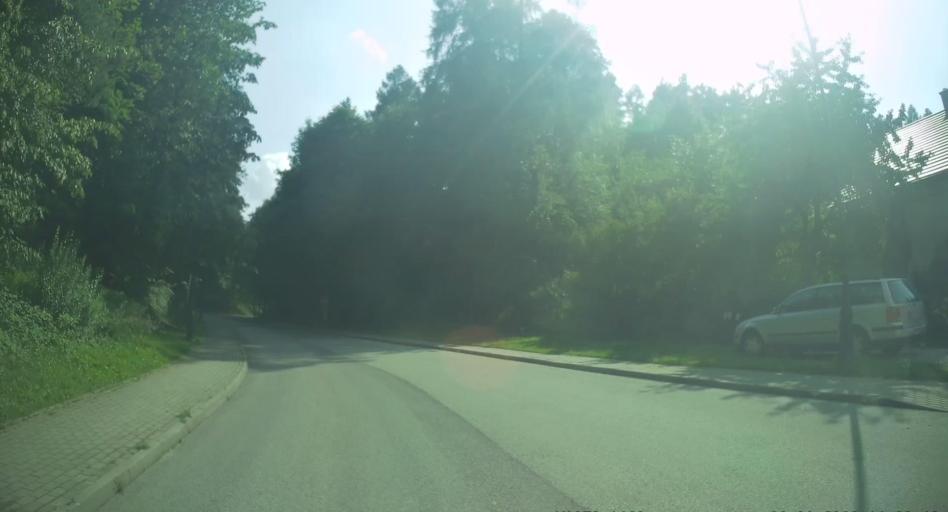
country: PL
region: Swietokrzyskie
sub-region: Powiat kielecki
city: Checiny
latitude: 50.7986
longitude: 20.4564
